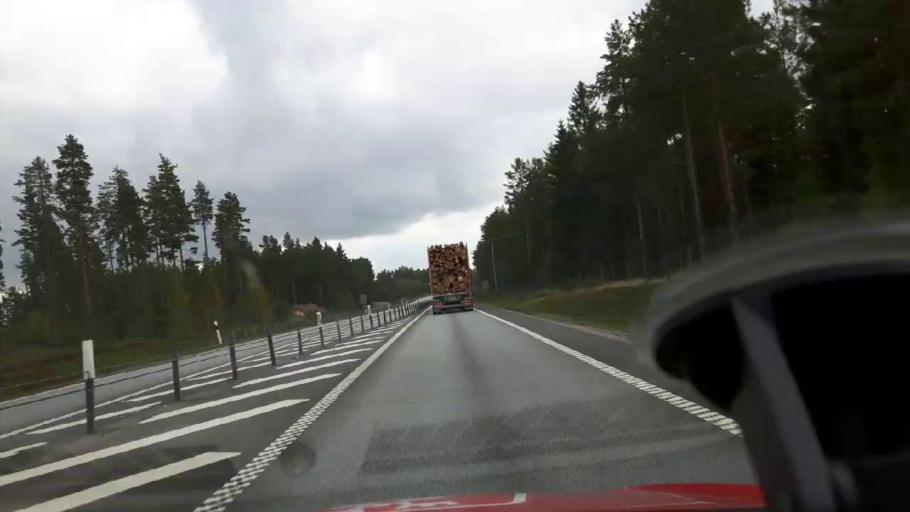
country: SE
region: Gaevleborg
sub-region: Gavle Kommun
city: Norrsundet
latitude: 61.0344
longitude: 16.9707
